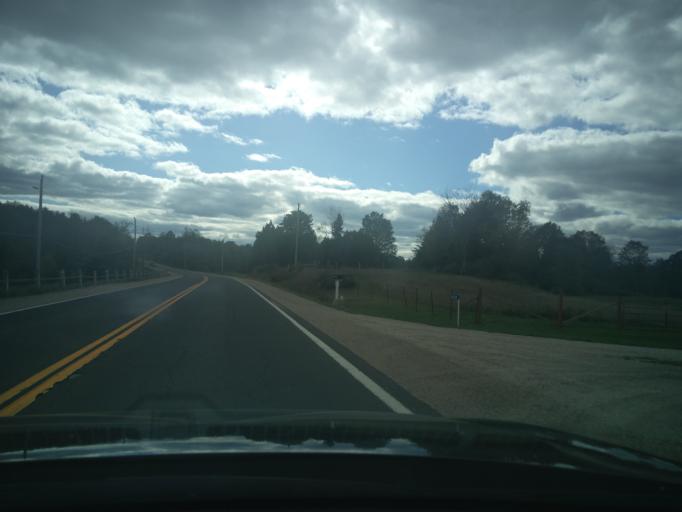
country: CA
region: Ontario
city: Perth
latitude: 44.8099
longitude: -76.3285
